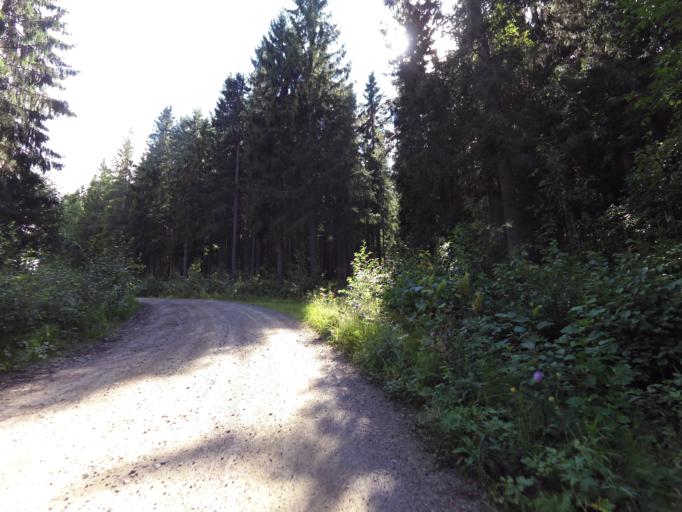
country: SE
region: Gaevleborg
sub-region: Hofors Kommun
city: Hofors
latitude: 60.5309
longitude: 16.2307
